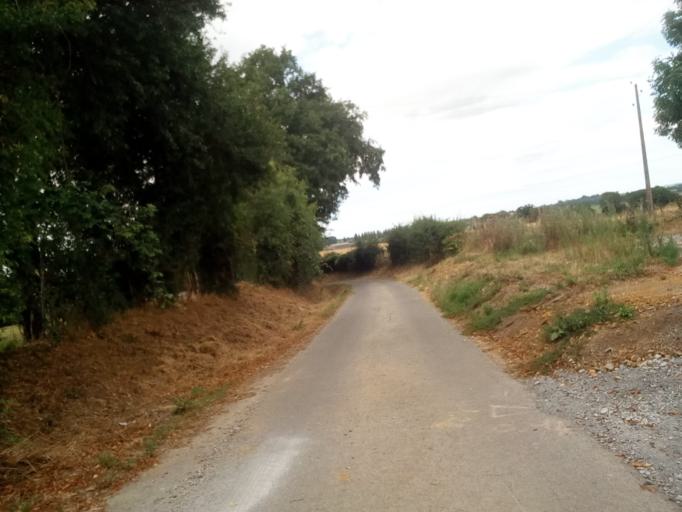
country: FR
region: Lower Normandy
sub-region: Departement du Calvados
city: Troarn
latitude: 49.1637
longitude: -0.1617
